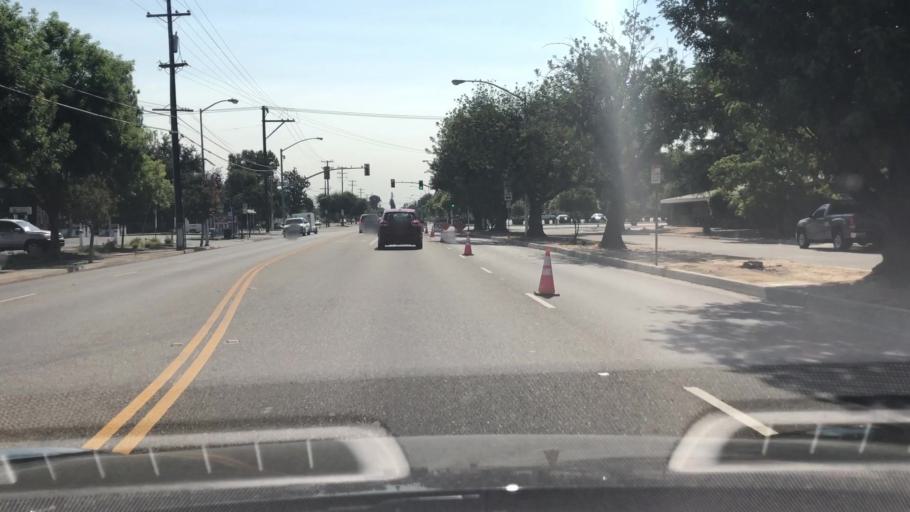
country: US
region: California
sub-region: Fresno County
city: Fresno
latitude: 36.7941
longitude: -119.7735
